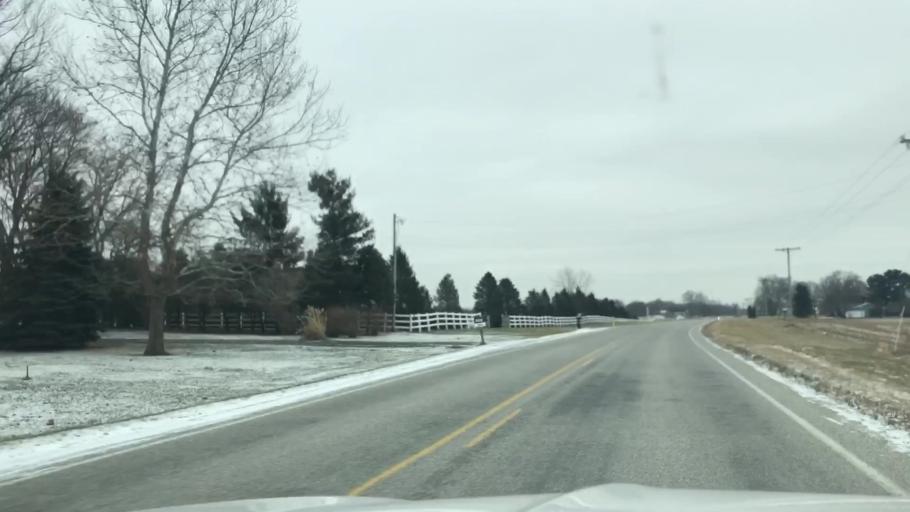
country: US
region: Indiana
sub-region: Fulton County
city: Rochester
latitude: 41.0365
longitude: -86.1999
